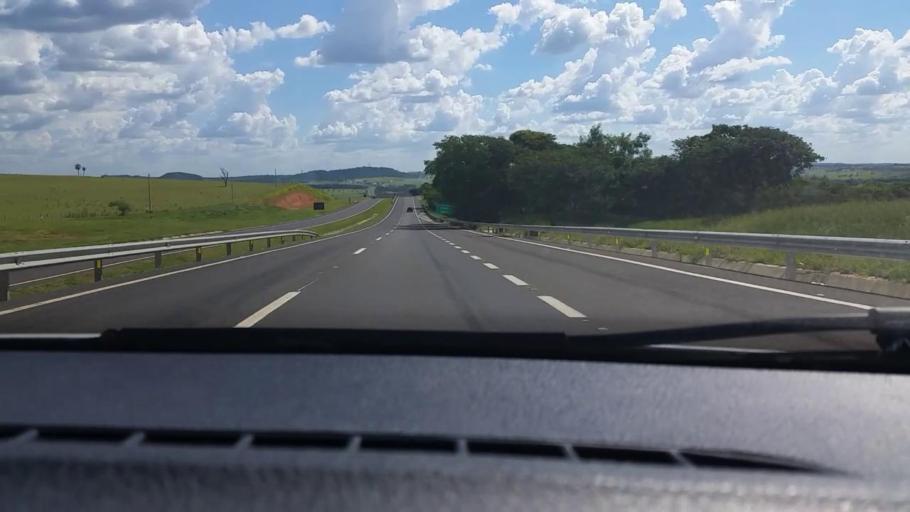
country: BR
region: Sao Paulo
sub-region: Bauru
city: Bauru
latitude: -22.3926
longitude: -49.0805
